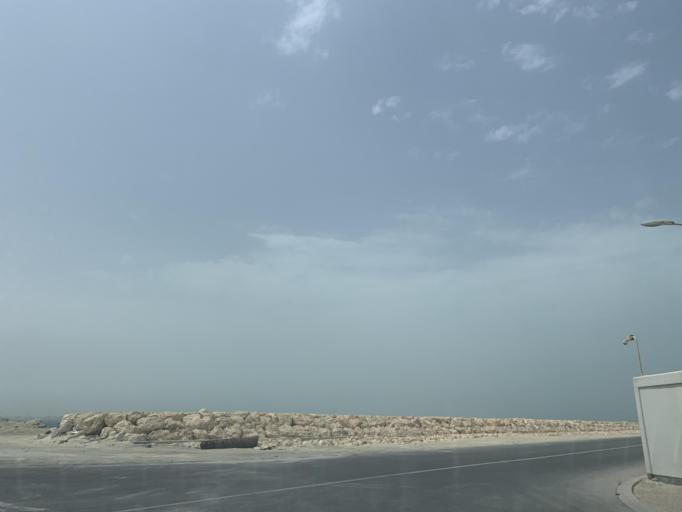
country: BH
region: Muharraq
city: Al Hadd
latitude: 26.2259
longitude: 50.7015
